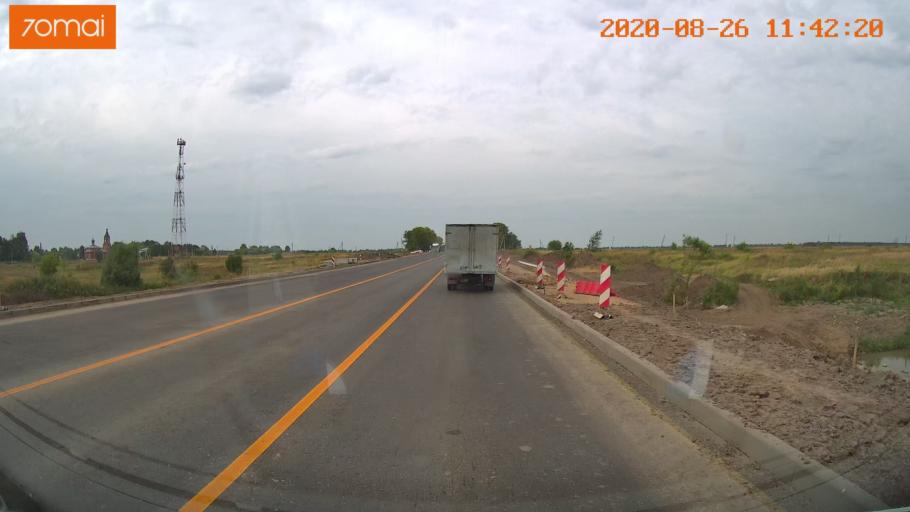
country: RU
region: Rjazan
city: Shilovo
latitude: 54.2975
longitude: 40.6949
